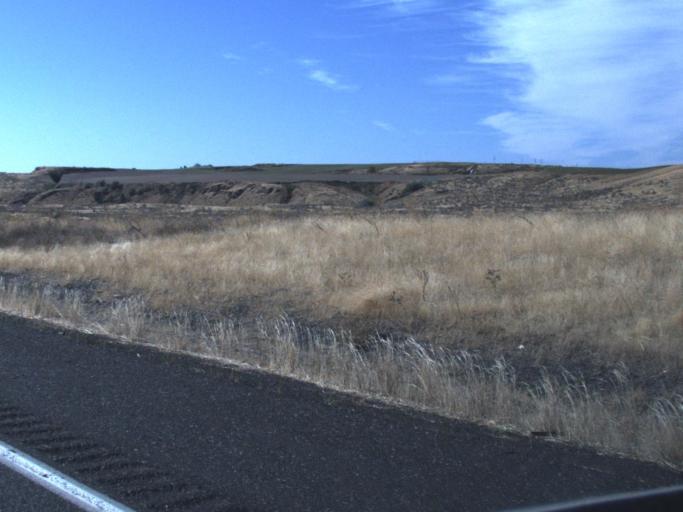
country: US
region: Washington
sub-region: Franklin County
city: Basin City
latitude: 46.5061
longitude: -119.0146
